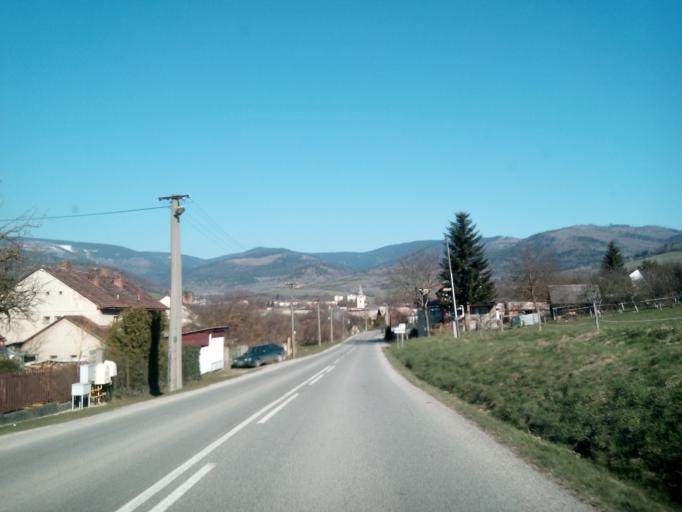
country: SK
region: Kosicky
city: Dobsina
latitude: 48.7089
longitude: 20.2898
